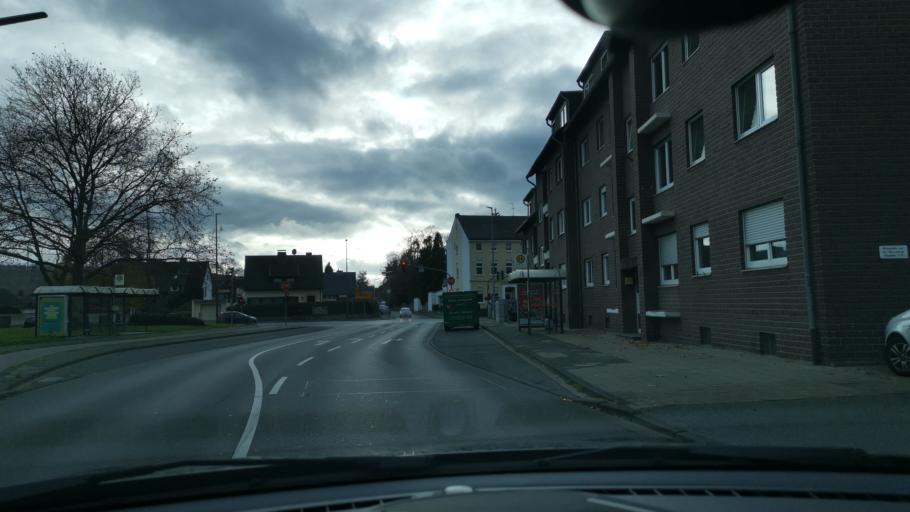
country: DE
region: North Rhine-Westphalia
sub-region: Regierungsbezirk Dusseldorf
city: Grevenbroich
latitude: 51.0871
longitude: 6.6027
